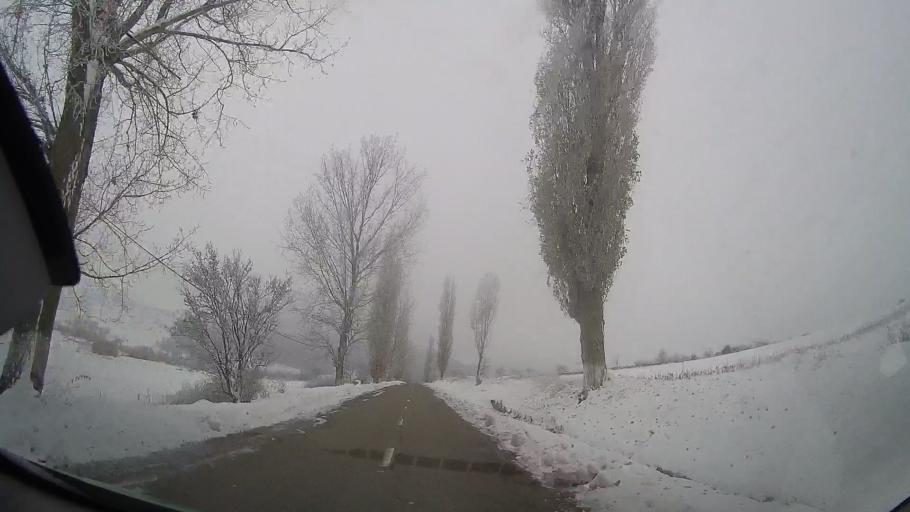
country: RO
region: Neamt
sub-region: Comuna Bozieni
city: Bozieni
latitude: 46.8414
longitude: 27.1682
